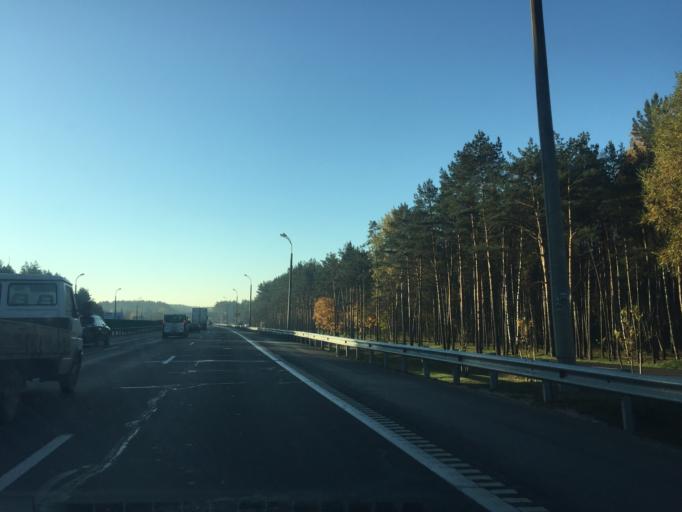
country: BY
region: Minsk
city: Vyaliki Trastsyanets
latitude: 53.8945
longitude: 27.6919
